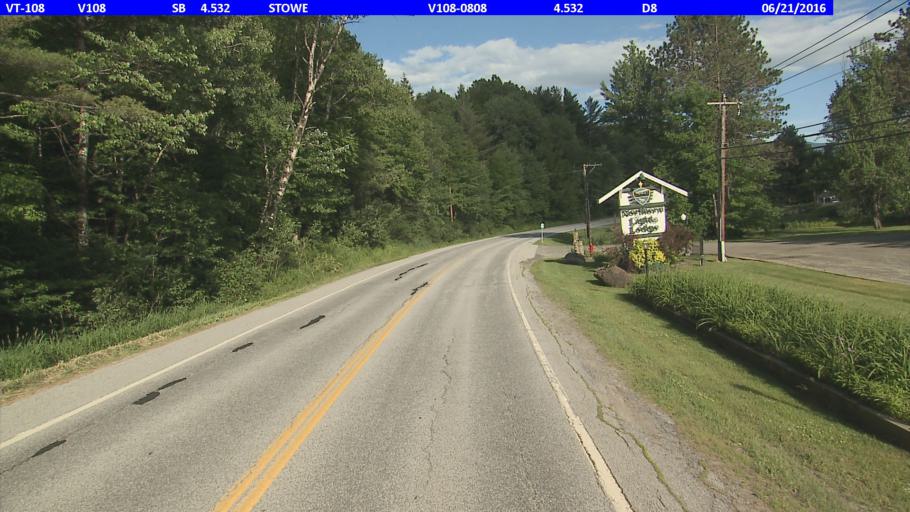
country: US
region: Vermont
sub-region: Lamoille County
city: Morristown
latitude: 44.4995
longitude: -72.7456
